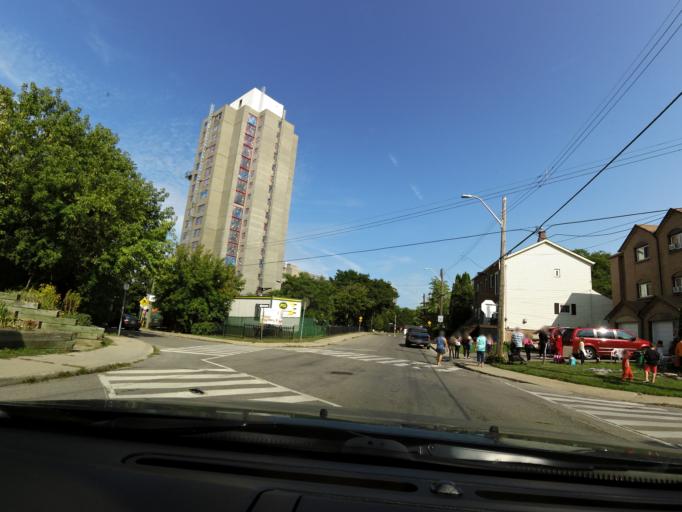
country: CA
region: Ontario
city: Hamilton
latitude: 43.2725
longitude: -79.8638
